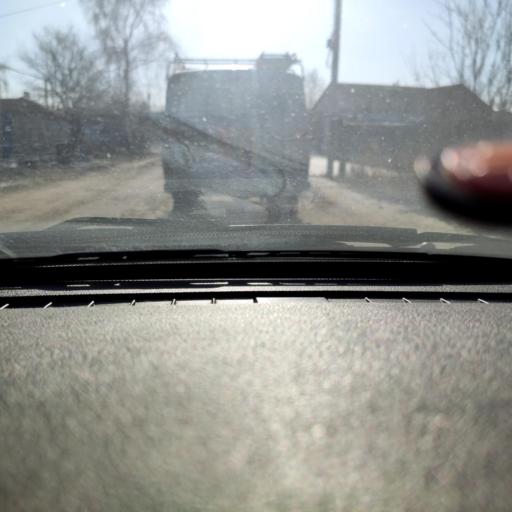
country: RU
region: Voronezj
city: Latnaya
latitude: 51.6932
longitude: 38.9477
